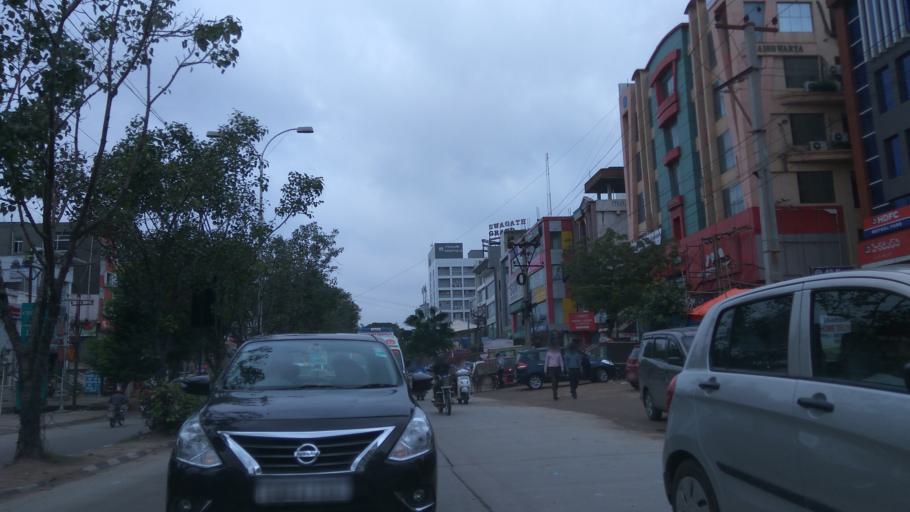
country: IN
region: Telangana
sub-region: Rangareddi
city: Secunderabad
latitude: 17.4817
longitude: 78.5543
